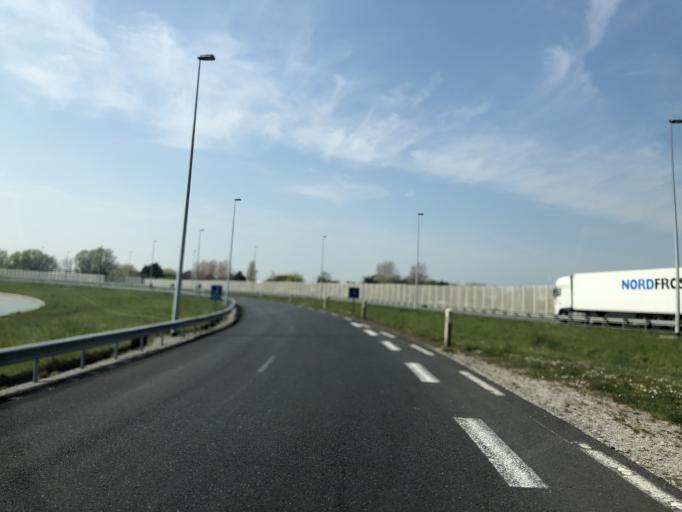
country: FR
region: Nord-Pas-de-Calais
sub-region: Departement du Pas-de-Calais
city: Coquelles
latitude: 50.9429
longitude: 1.8171
